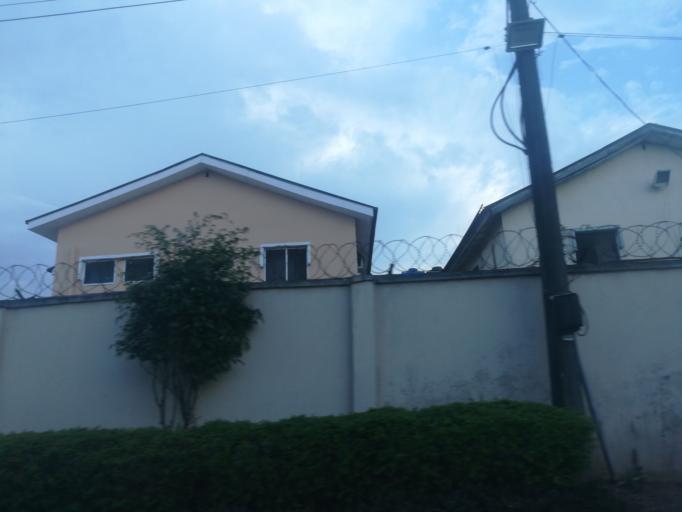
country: NG
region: Lagos
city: Somolu
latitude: 6.5545
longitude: 3.3775
